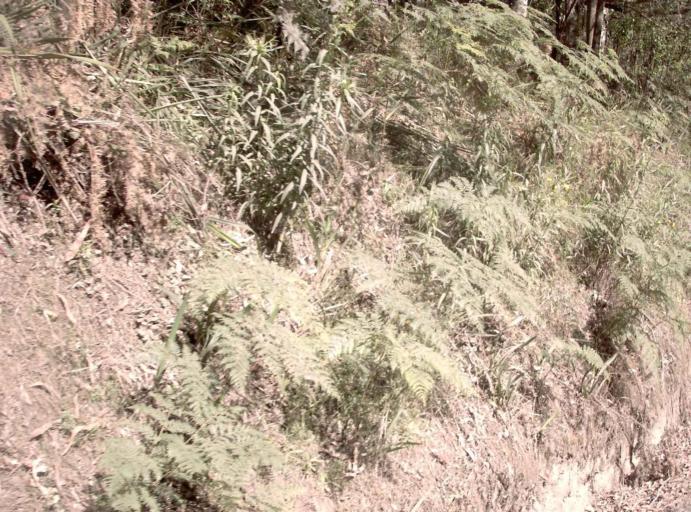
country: AU
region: New South Wales
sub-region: Bombala
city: Bombala
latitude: -37.2189
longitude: 148.7469
